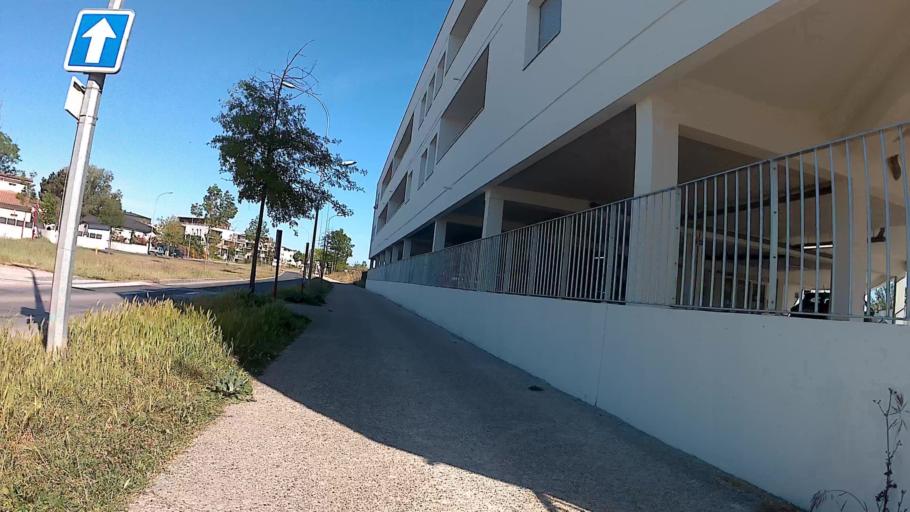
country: FR
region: Aquitaine
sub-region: Departement de la Gironde
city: Villenave-d'Ornon
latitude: 44.7752
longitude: -0.5287
